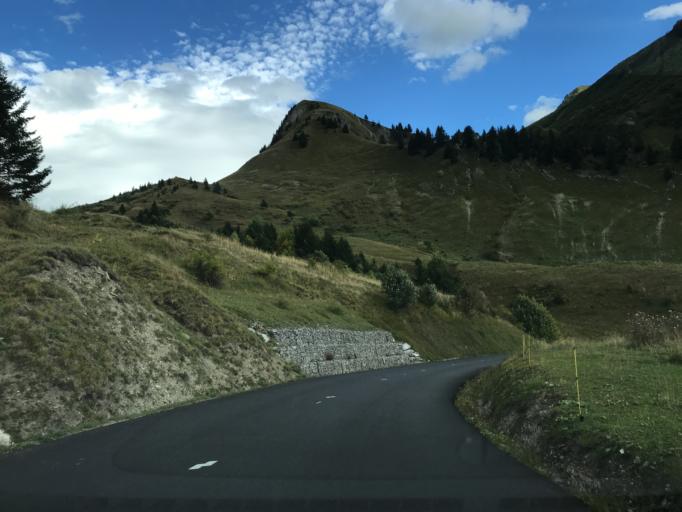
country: FR
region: Rhone-Alpes
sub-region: Departement de la Haute-Savoie
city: Le Grand-Bornand
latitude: 45.9892
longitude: 6.4695
